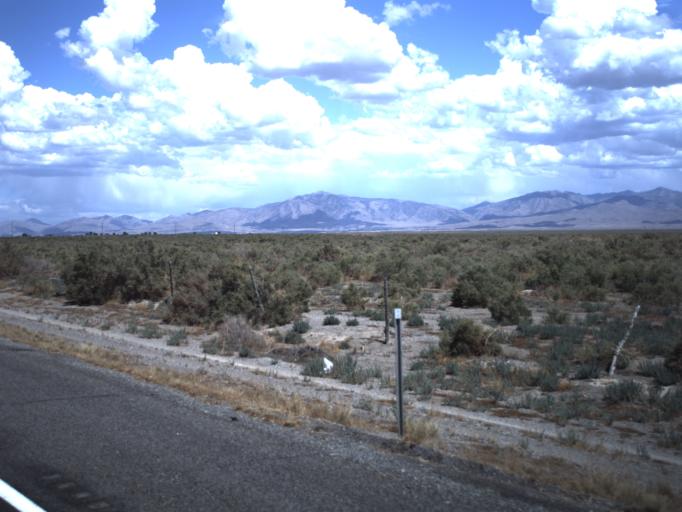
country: US
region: Utah
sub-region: Millard County
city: Delta
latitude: 39.3655
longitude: -112.5474
